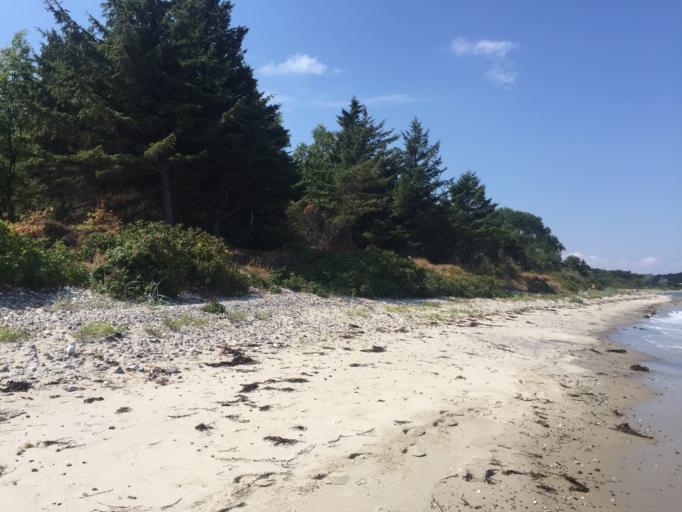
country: DK
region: Central Jutland
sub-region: Samso Kommune
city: Tranebjerg
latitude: 55.9574
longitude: 10.4339
